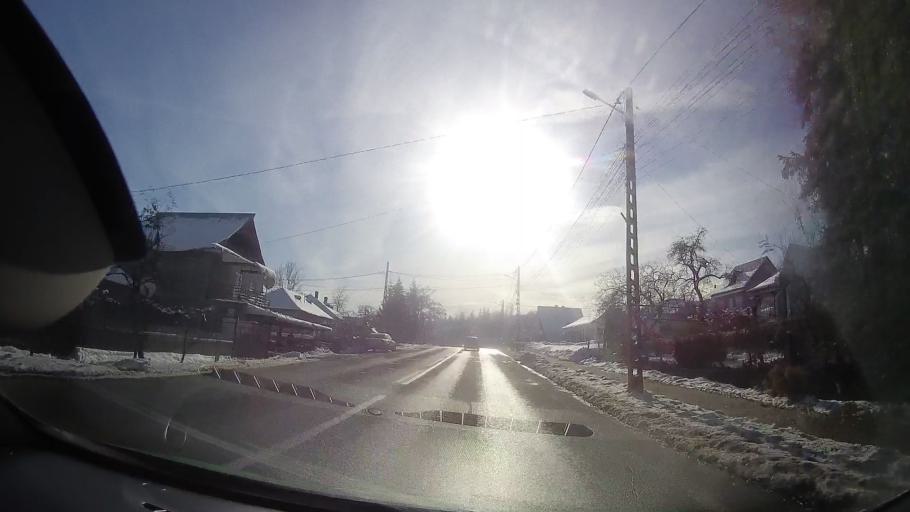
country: RO
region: Neamt
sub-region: Comuna Baltatesti
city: Baltatesti
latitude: 47.1241
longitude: 26.3103
